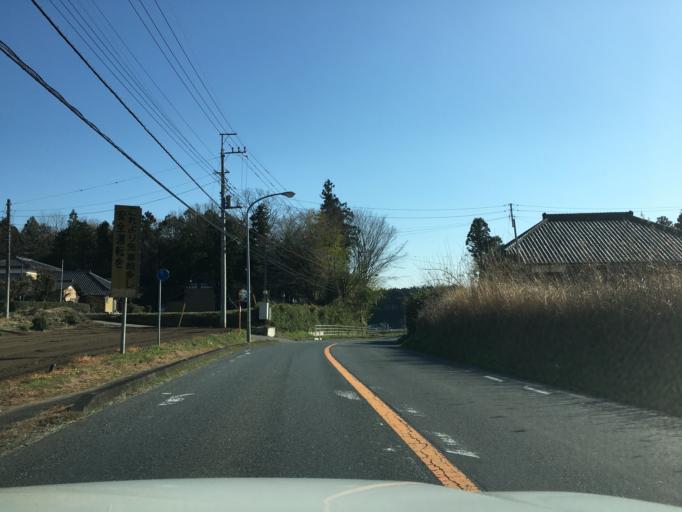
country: JP
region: Ibaraki
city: Omiya
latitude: 36.4564
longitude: 140.4070
